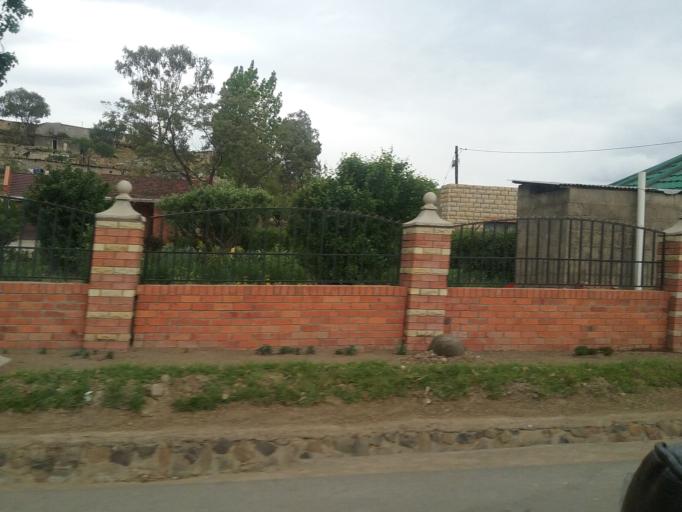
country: LS
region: Maseru
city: Maseru
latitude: -29.3292
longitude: 27.5071
